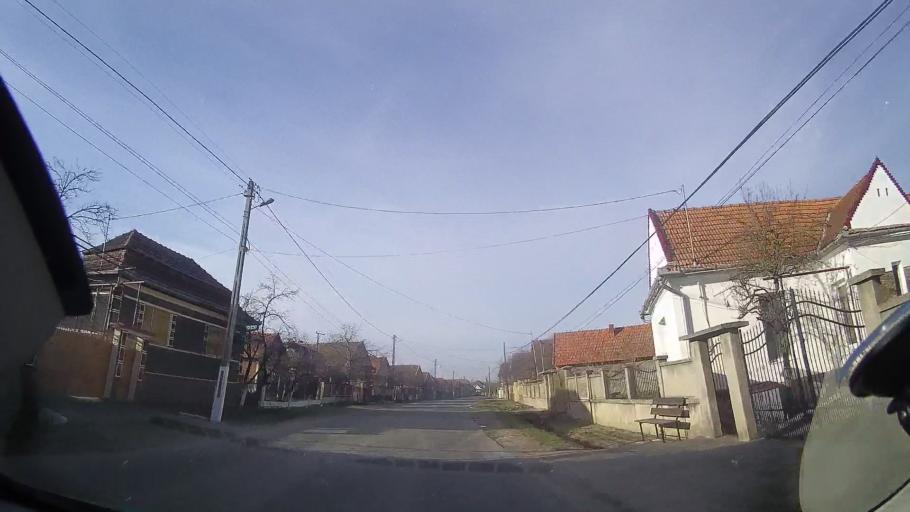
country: RO
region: Bihor
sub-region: Comuna Brusturi
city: Brusturi
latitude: 47.1546
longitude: 22.2437
